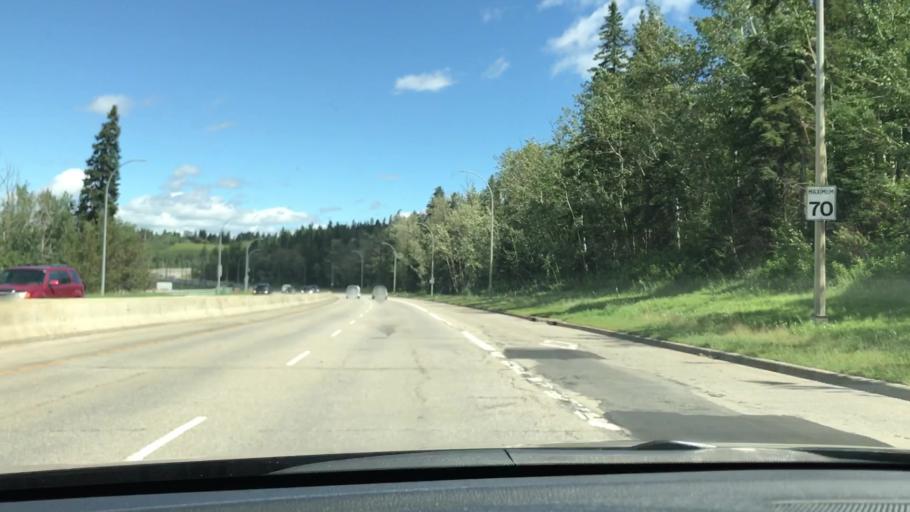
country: CA
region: Alberta
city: Edmonton
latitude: 53.5032
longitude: -113.5548
